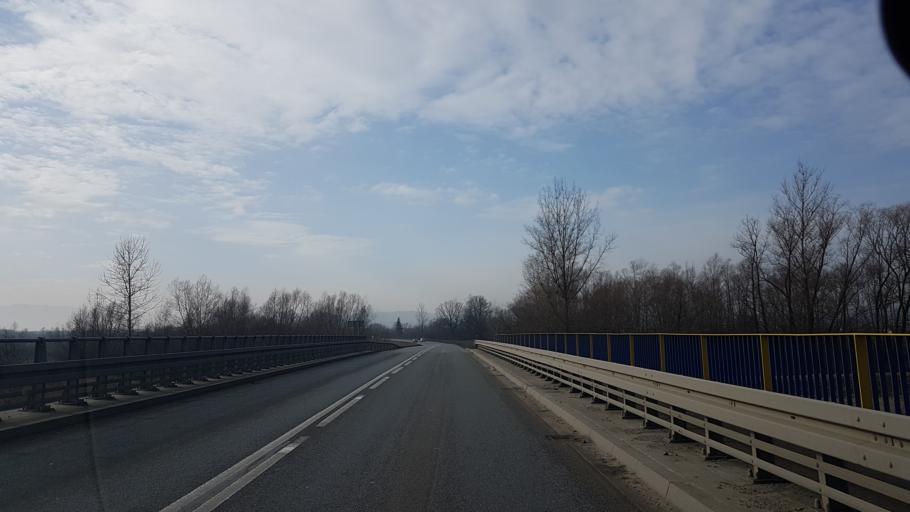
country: PL
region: Lesser Poland Voivodeship
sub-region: Powiat nowosadecki
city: Stary Sacz
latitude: 49.5862
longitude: 20.6250
